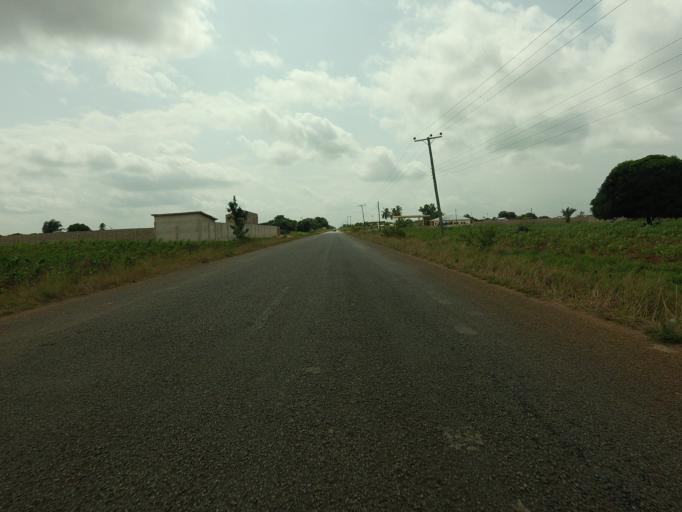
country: TG
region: Maritime
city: Lome
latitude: 6.1799
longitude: 1.0684
